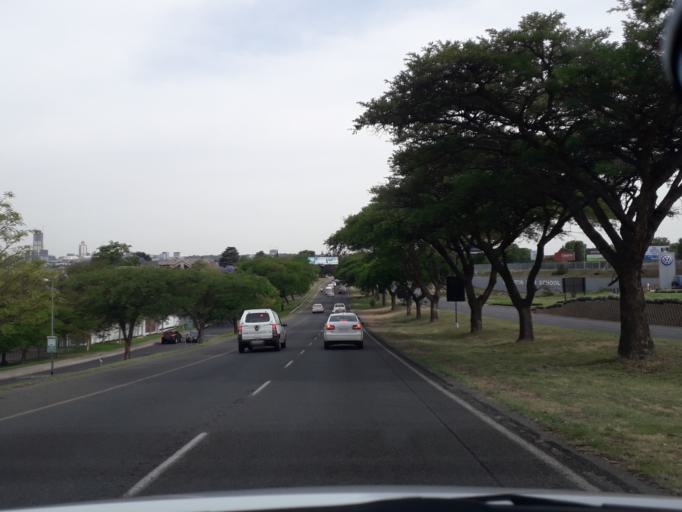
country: ZA
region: Gauteng
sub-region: City of Johannesburg Metropolitan Municipality
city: Midrand
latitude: -26.0688
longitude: 28.0258
